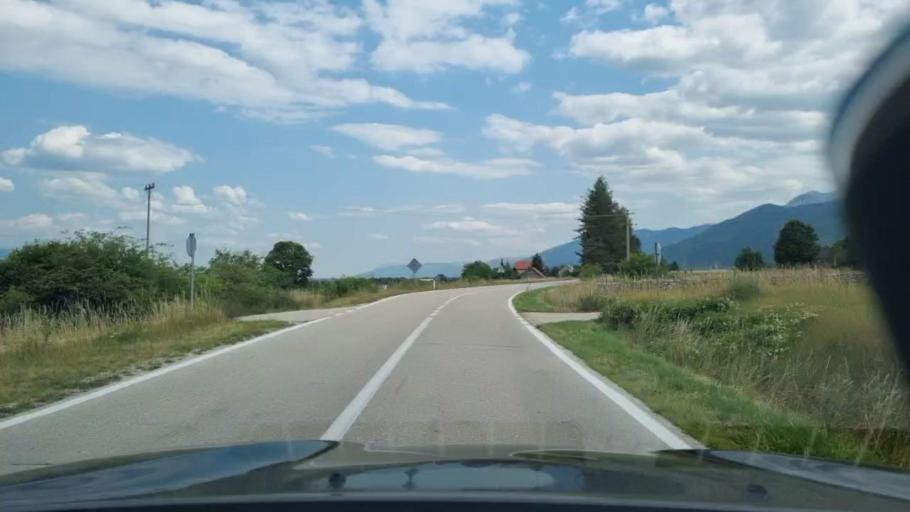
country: BA
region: Federation of Bosnia and Herzegovina
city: Glamoc
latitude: 44.0375
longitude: 16.5944
